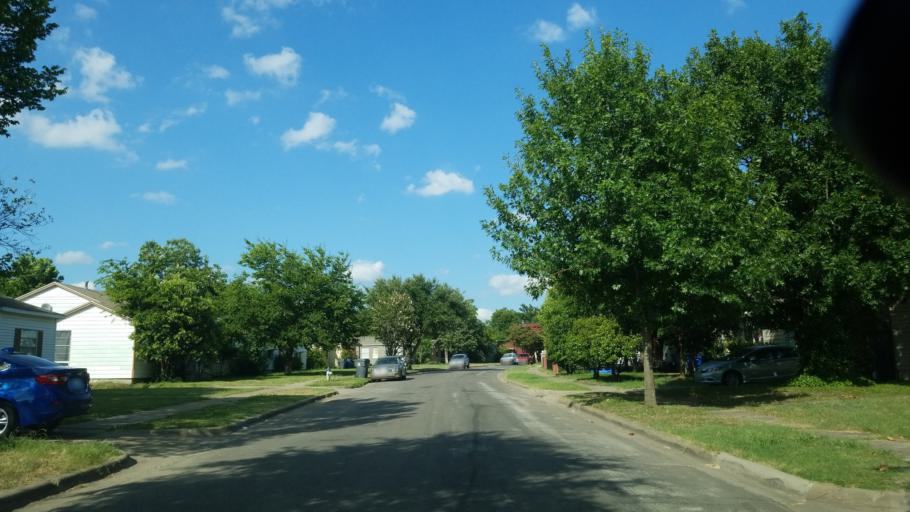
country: US
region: Texas
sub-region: Dallas County
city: Balch Springs
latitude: 32.7663
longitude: -96.7106
